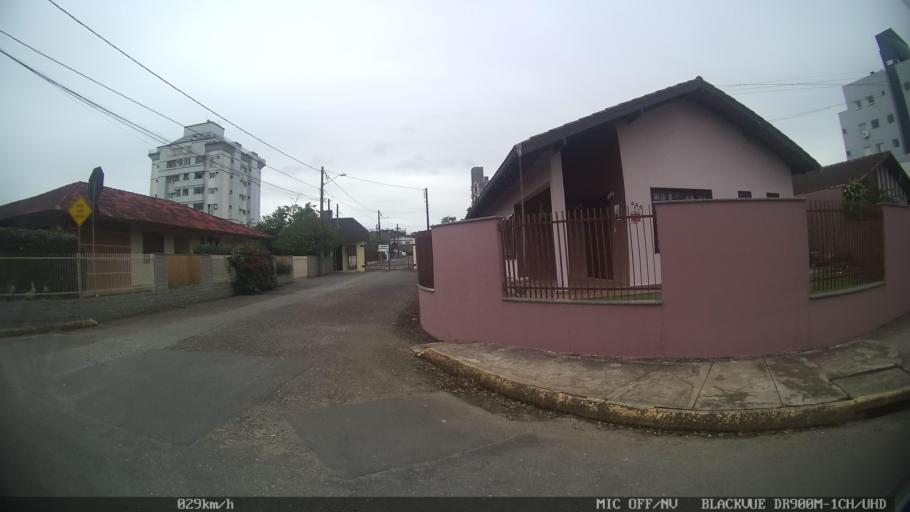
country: BR
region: Santa Catarina
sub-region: Joinville
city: Joinville
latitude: -26.2655
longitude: -48.8471
